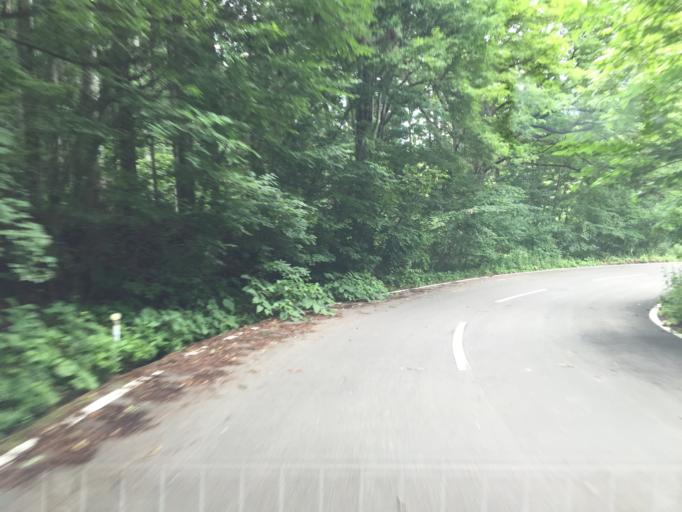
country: JP
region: Fukushima
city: Nihommatsu
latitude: 37.6726
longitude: 140.3309
